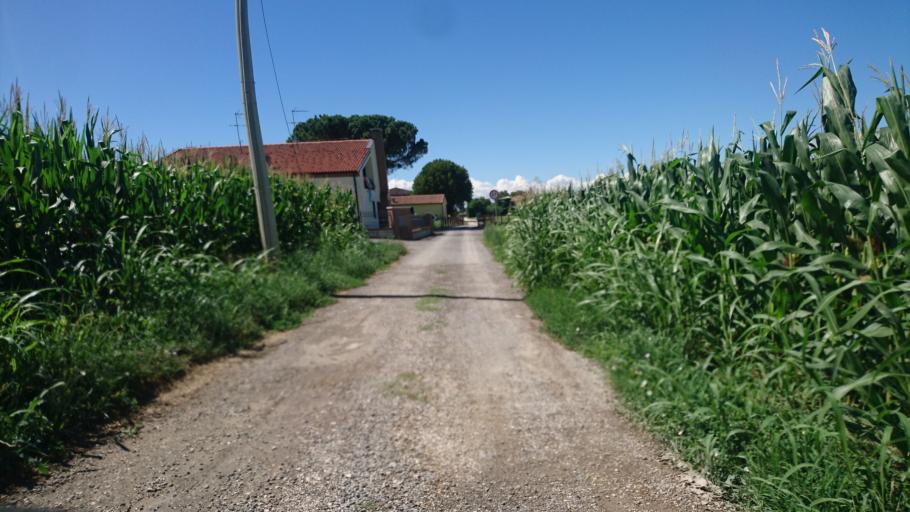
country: IT
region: Veneto
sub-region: Provincia di Padova
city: Pontelongo
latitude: 45.2555
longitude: 12.0188
